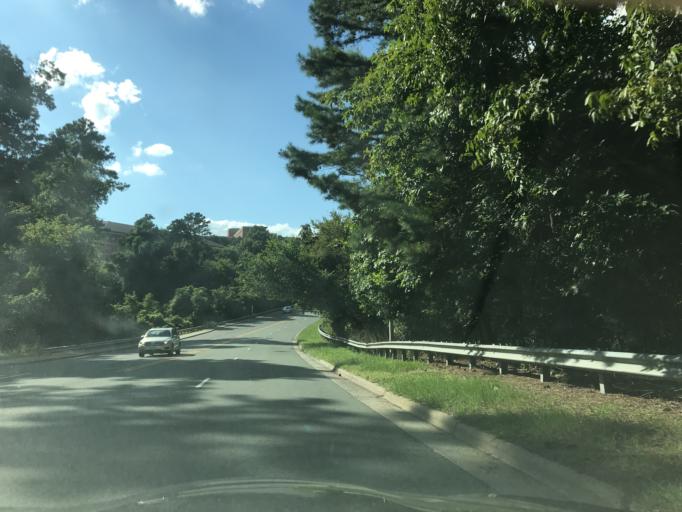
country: US
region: North Carolina
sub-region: Orange County
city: Chapel Hill
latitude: 35.9009
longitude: -79.0397
